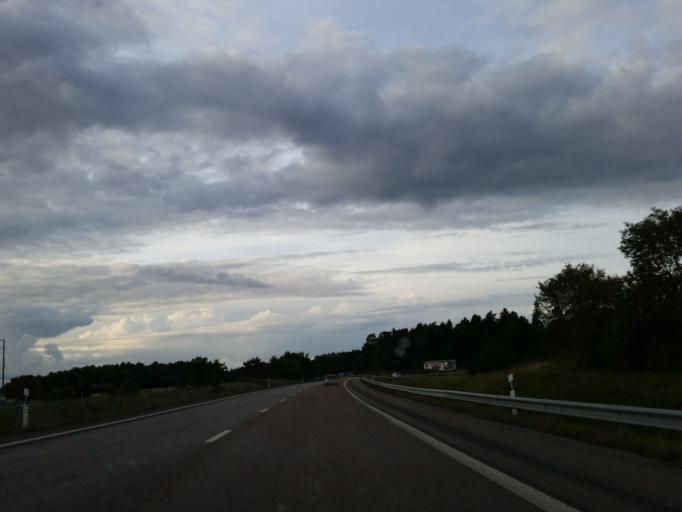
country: SE
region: Uppsala
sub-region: Knivsta Kommun
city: Knivsta
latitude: 59.7415
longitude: 17.8189
